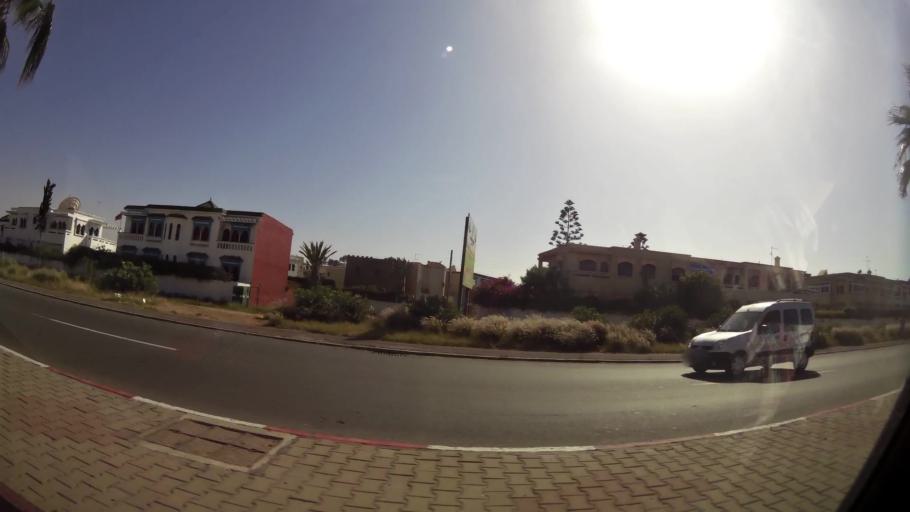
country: MA
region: Souss-Massa-Draa
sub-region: Inezgane-Ait Mellou
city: Inezgane
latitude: 30.3771
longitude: -9.5591
